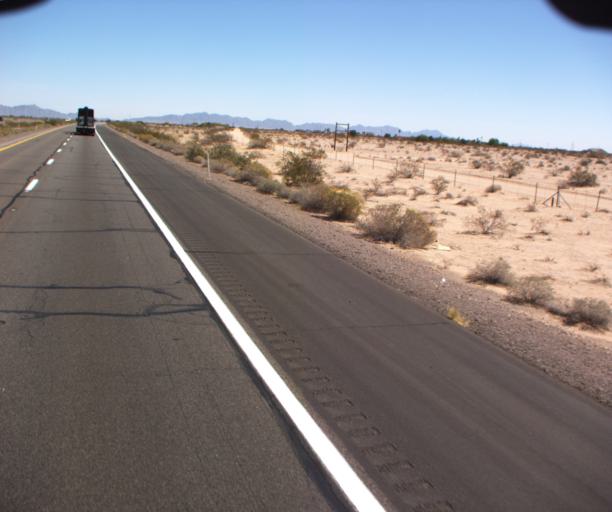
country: US
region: Arizona
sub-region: Yuma County
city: Wellton
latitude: 32.6861
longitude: -113.9996
